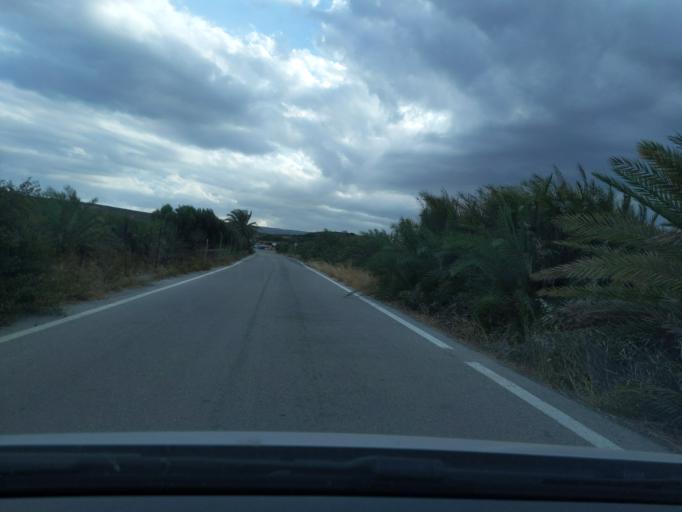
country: GR
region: Crete
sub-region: Nomos Lasithiou
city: Palekastro
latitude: 35.2559
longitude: 26.2539
